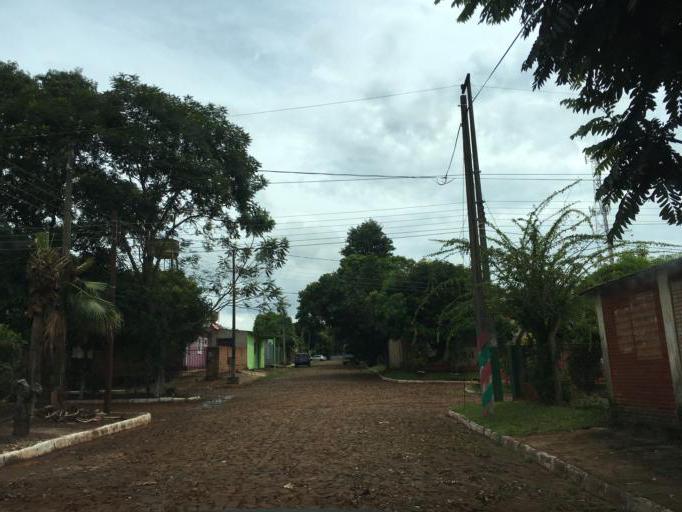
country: PY
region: Alto Parana
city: Ciudad del Este
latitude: -25.4175
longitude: -54.6390
